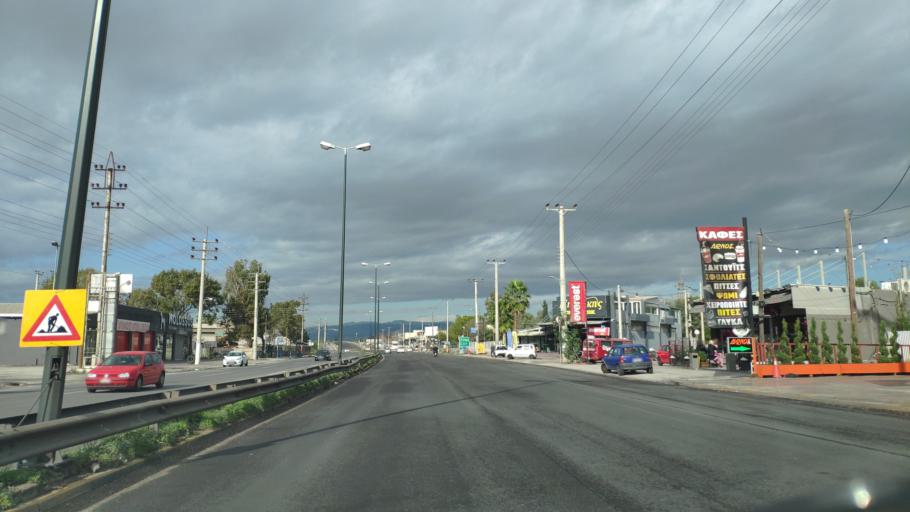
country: GR
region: Attica
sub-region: Nomarchia Dytikis Attikis
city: Aspropyrgos
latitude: 38.0384
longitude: 23.5915
